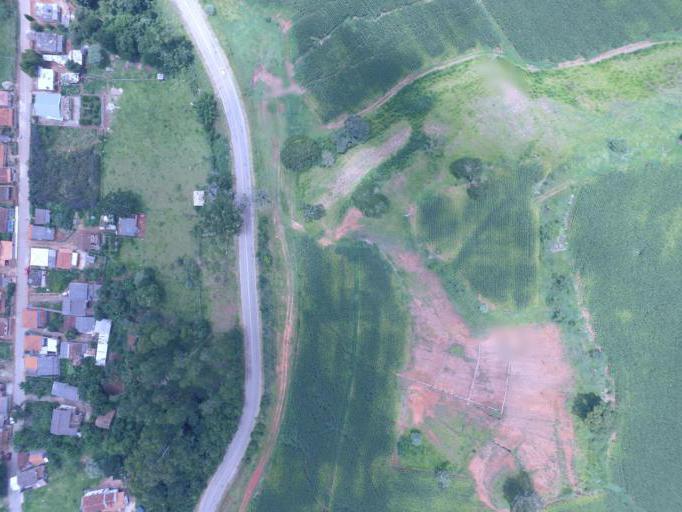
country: BR
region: Minas Gerais
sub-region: Tiradentes
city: Tiradentes
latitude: -21.0862
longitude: -44.0751
